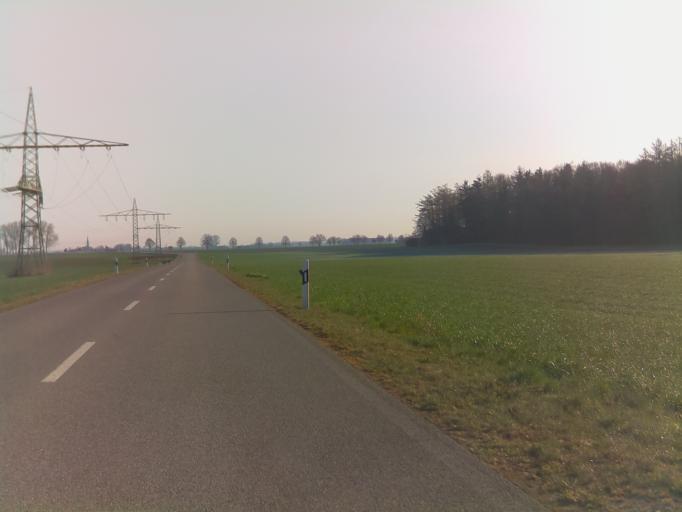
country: DE
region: Bavaria
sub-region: Upper Bavaria
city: Scheuring
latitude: 48.1433
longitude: 10.8755
